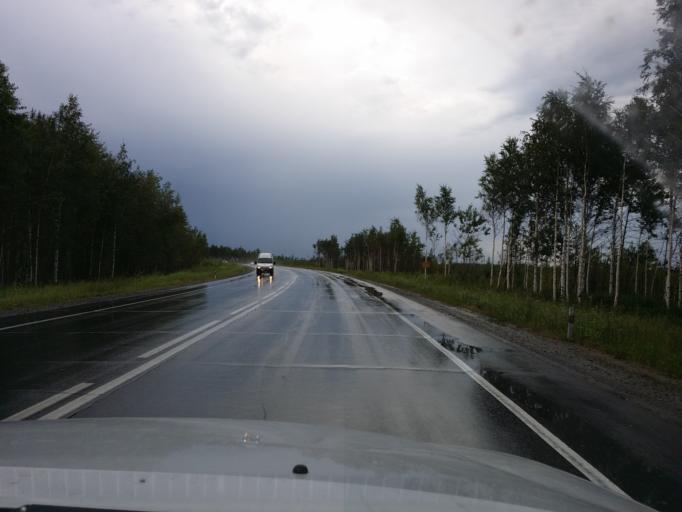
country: RU
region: Khanty-Mansiyskiy Avtonomnyy Okrug
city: Megion
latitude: 61.0682
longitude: 76.2497
